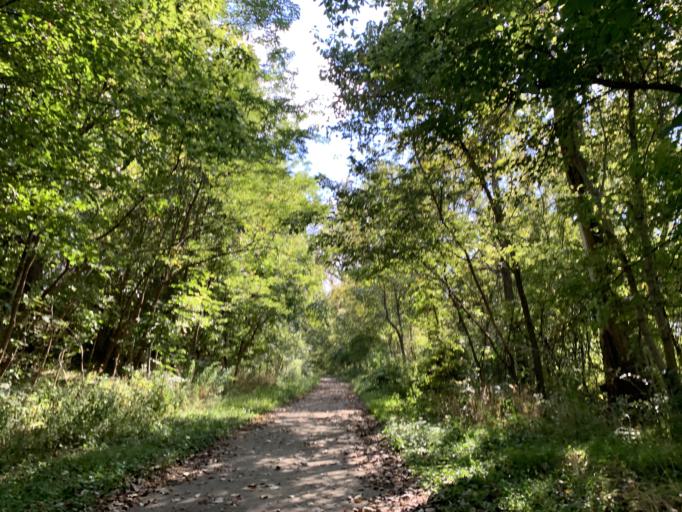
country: US
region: Indiana
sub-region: Floyd County
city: New Albany
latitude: 38.2572
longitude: -85.8323
